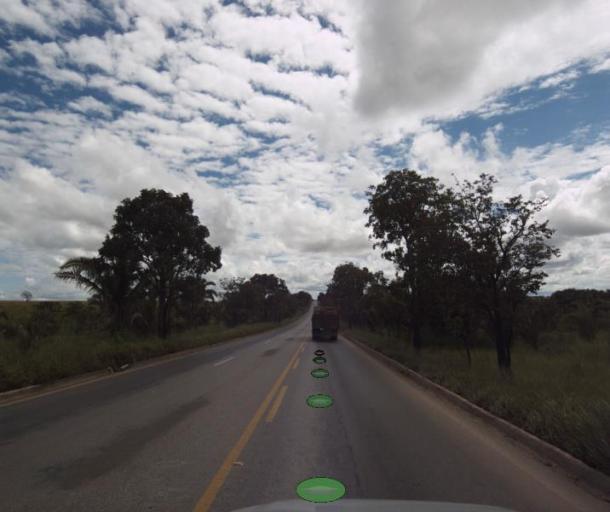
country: BR
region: Goias
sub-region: Uruacu
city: Uruacu
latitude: -14.3797
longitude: -49.1580
